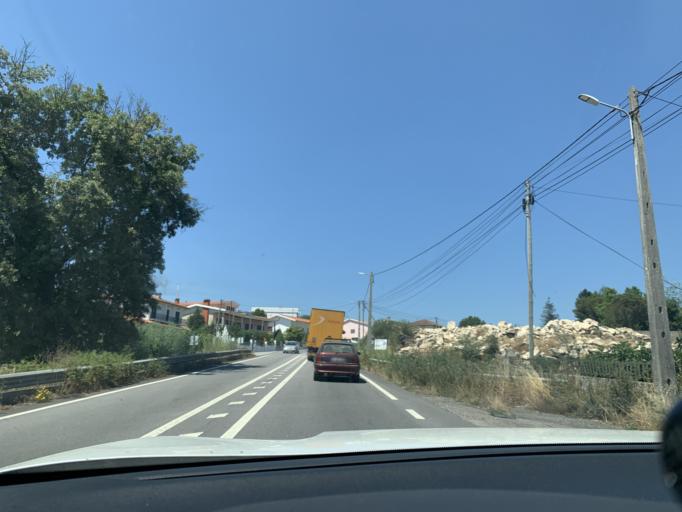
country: PT
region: Viseu
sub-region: Mangualde
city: Mangualde
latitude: 40.5988
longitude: -7.7919
